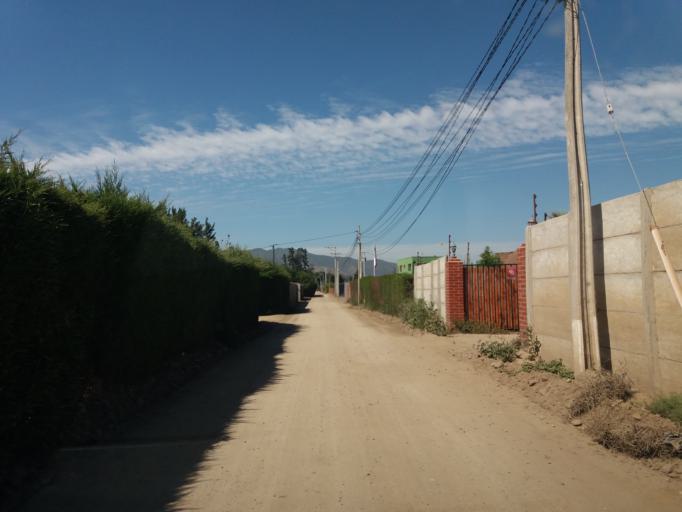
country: CL
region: Valparaiso
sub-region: Provincia de Quillota
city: Quillota
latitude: -32.8714
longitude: -71.2240
